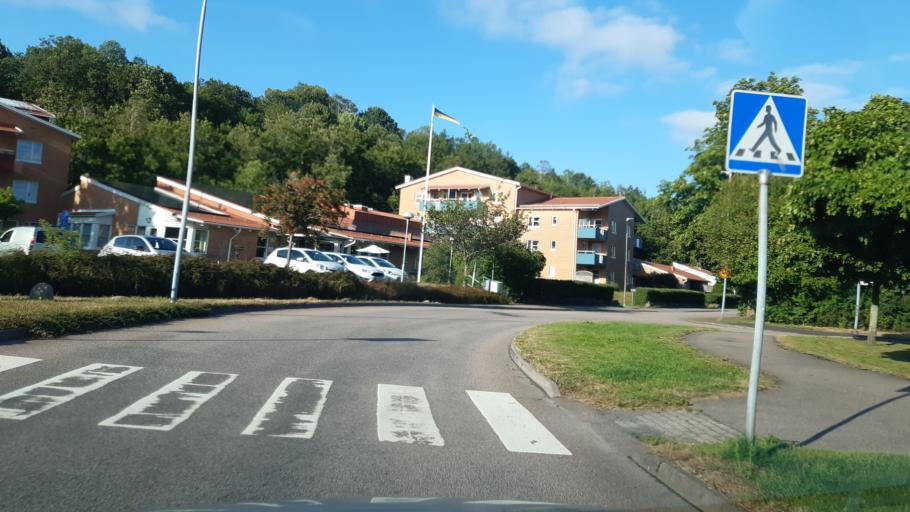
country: SE
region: Vaestra Goetaland
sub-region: Partille Kommun
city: Partille
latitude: 57.7212
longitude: 12.0656
